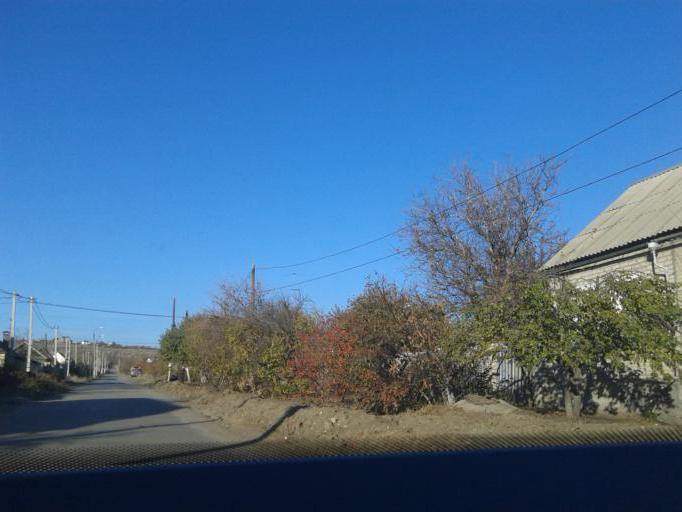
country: RU
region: Volgograd
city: Volgograd
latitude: 48.6110
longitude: 44.4174
